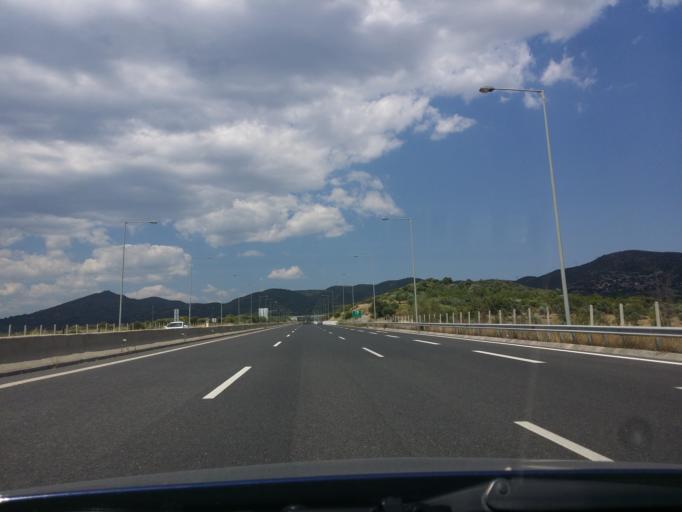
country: GR
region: Peloponnese
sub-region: Nomos Arkadias
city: Megalopoli
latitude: 37.3858
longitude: 22.1683
